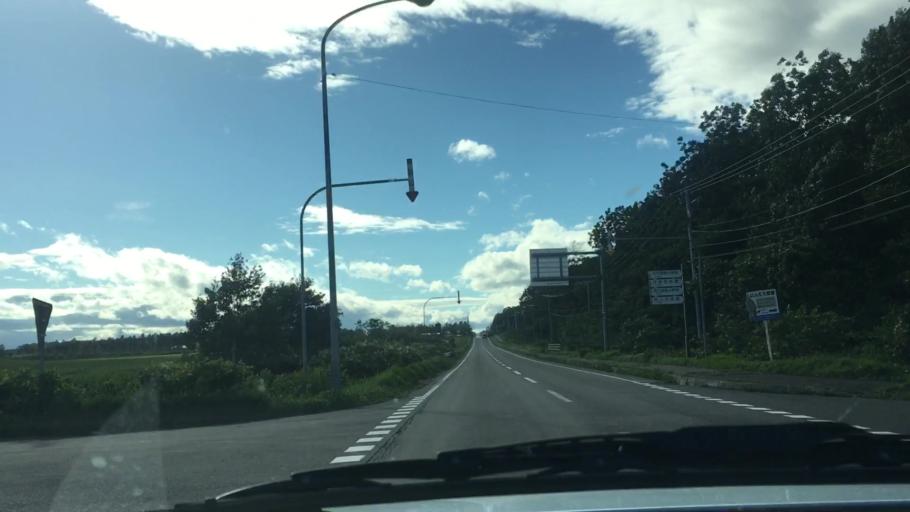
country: JP
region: Hokkaido
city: Otofuke
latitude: 43.1555
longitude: 143.1904
